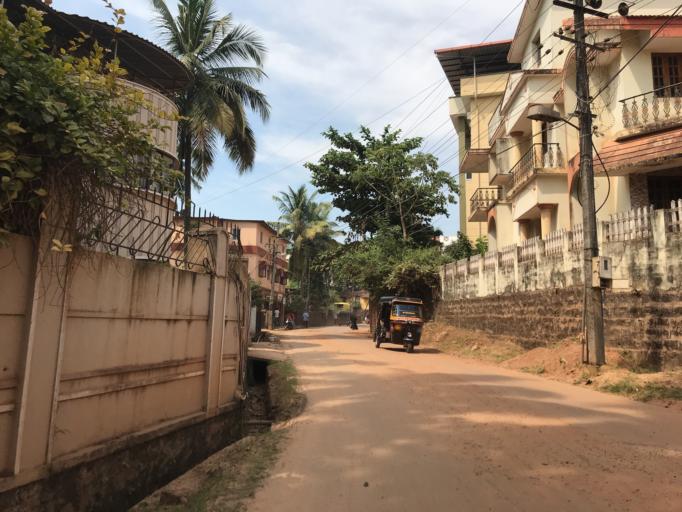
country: IN
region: Karnataka
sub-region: Dakshina Kannada
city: Ullal
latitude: 12.8457
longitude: 74.8469
